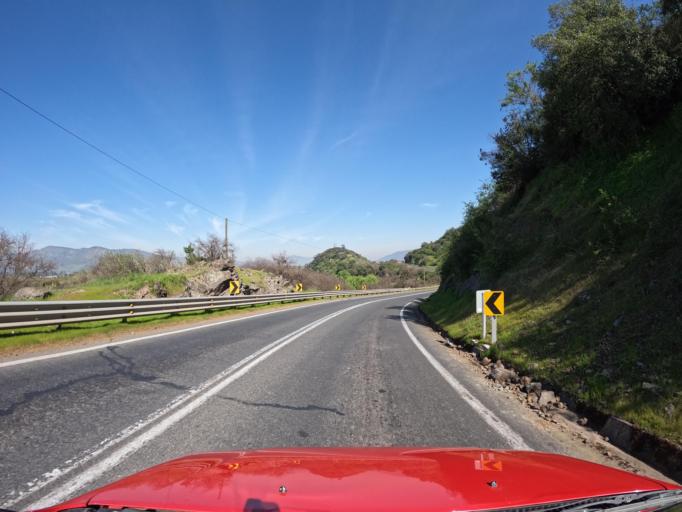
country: CL
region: Maule
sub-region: Provincia de Curico
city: Rauco
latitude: -34.9764
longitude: -71.3847
